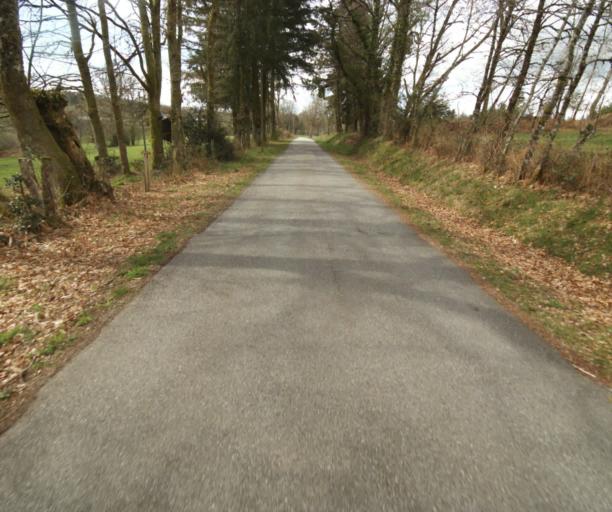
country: FR
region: Limousin
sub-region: Departement de la Correze
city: Correze
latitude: 45.3895
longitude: 1.8977
